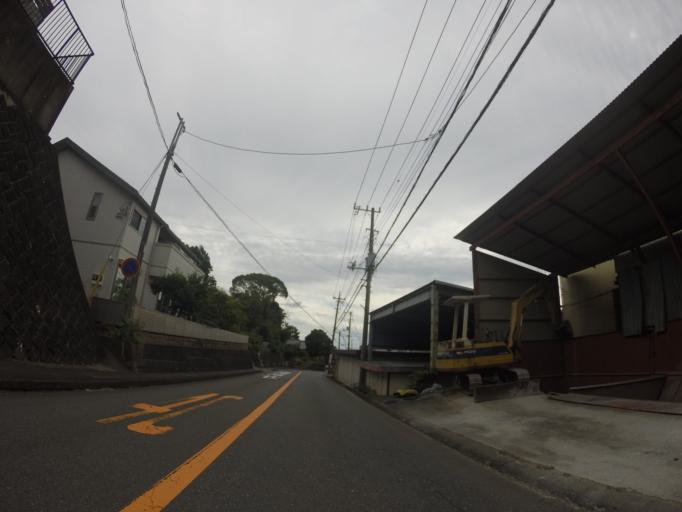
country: JP
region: Shizuoka
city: Fuji
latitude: 35.1897
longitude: 138.6902
